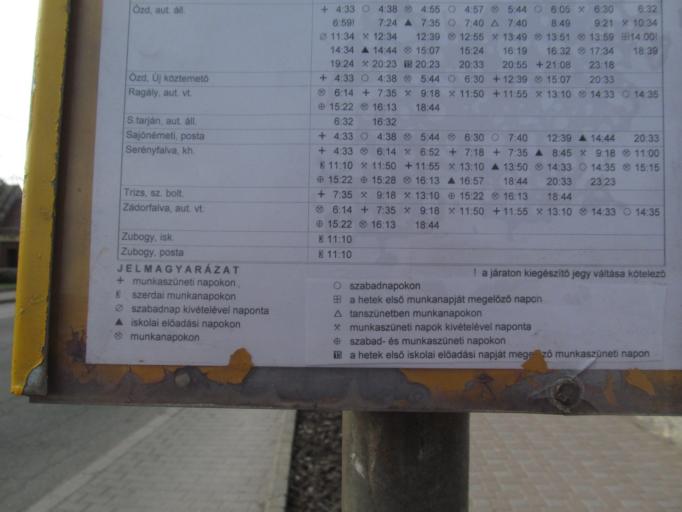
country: HU
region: Borsod-Abauj-Zemplen
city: Putnok
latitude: 48.2949
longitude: 20.4327
